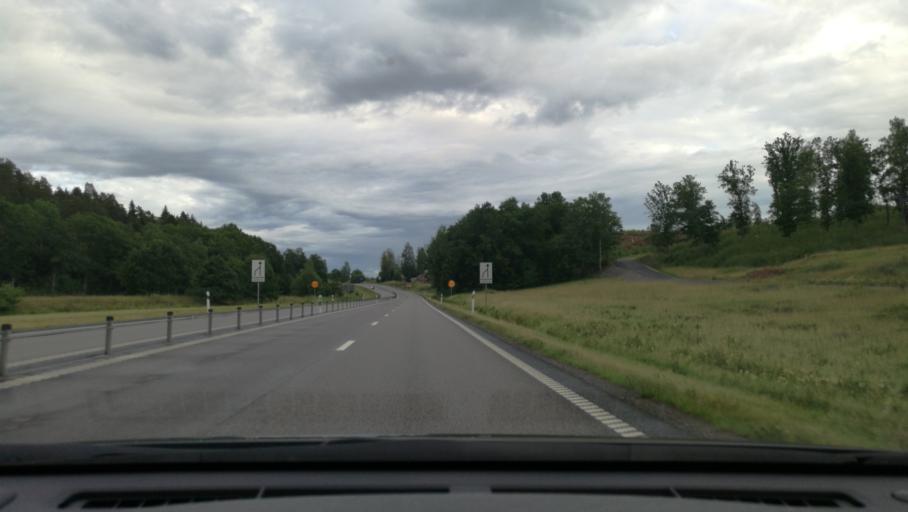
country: SE
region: OEstergoetland
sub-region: Norrkopings Kommun
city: Svartinge
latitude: 58.6899
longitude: 15.9273
